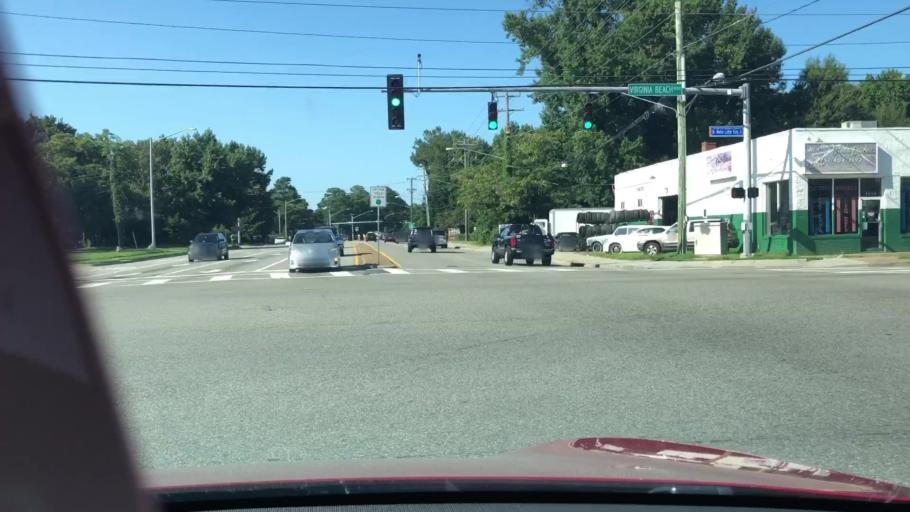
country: US
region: Virginia
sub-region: City of Virginia Beach
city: Virginia Beach
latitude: 36.8418
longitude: -75.9960
